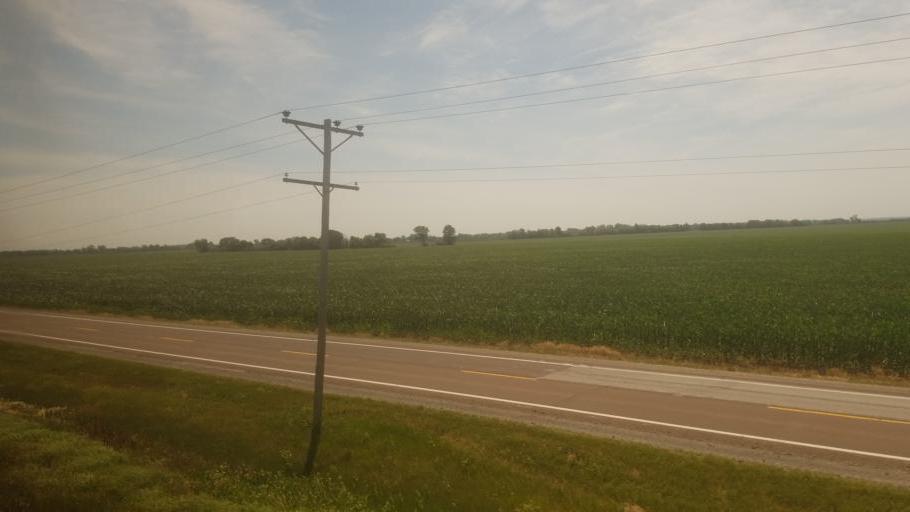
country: US
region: Missouri
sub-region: Carroll County
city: Carrollton
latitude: 39.3188
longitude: -93.6055
